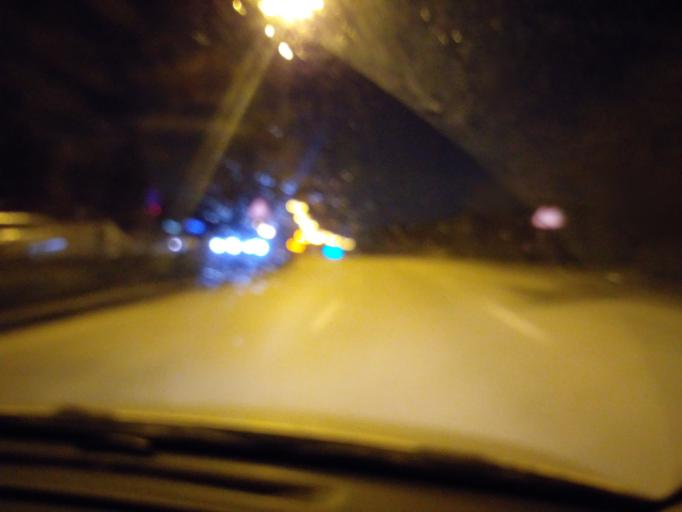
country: TR
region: Ankara
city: Batikent
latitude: 39.8878
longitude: 32.7193
